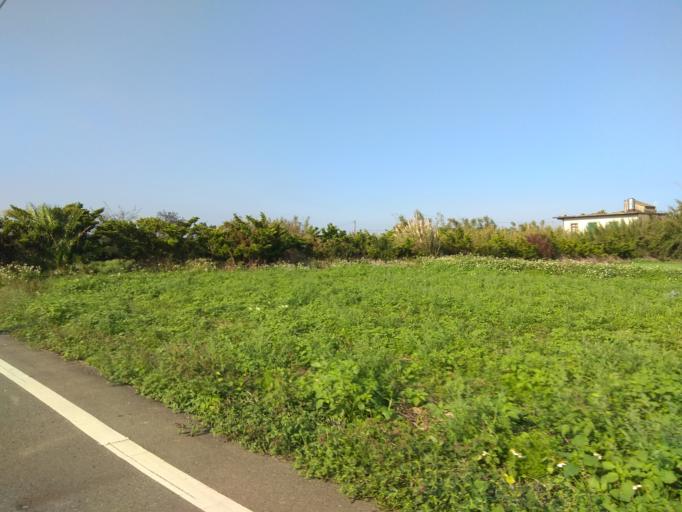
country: TW
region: Taiwan
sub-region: Hsinchu
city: Zhubei
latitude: 24.9958
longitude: 121.0401
